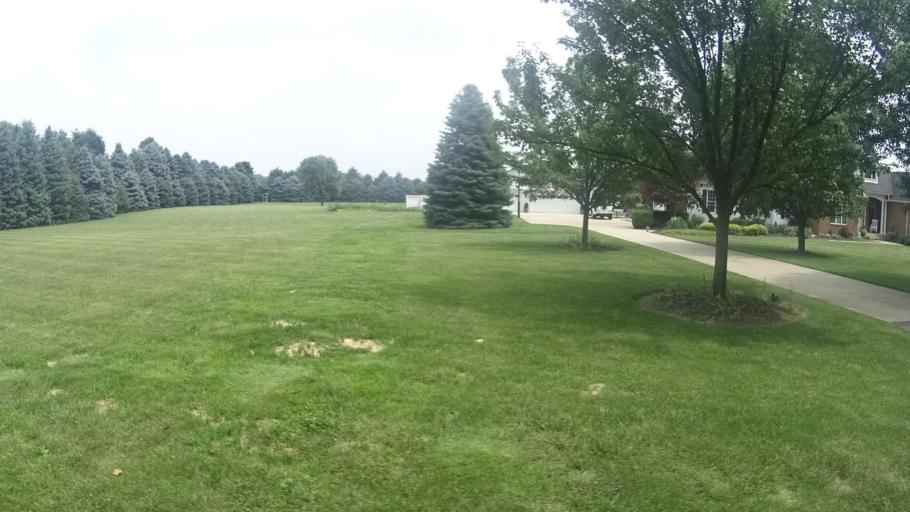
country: US
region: Ohio
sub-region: Erie County
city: Milan
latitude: 41.3014
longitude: -82.6318
